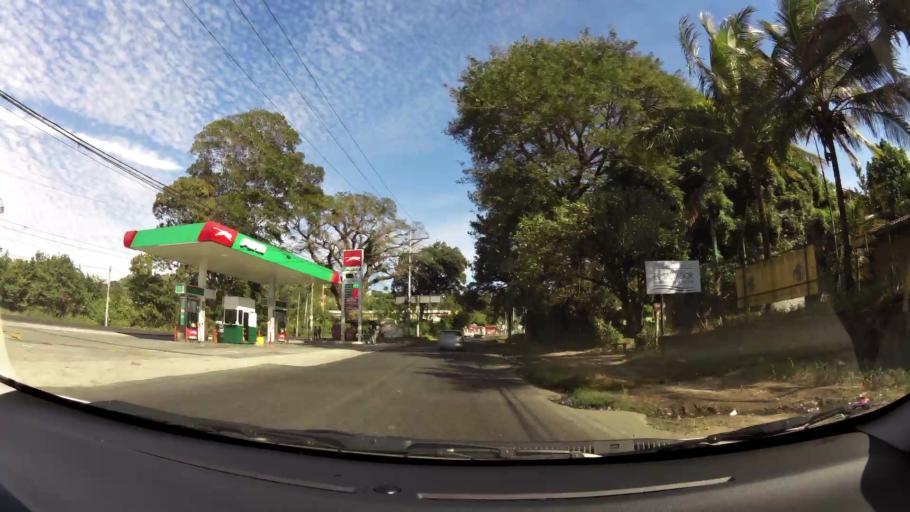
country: SV
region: Santa Ana
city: Santa Ana
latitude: 13.9848
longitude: -89.5884
